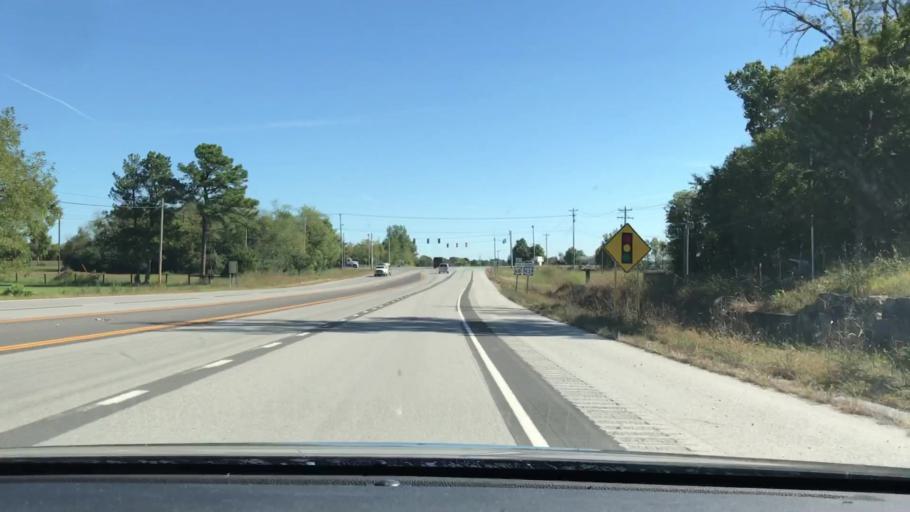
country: US
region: Kentucky
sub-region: Logan County
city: Russellville
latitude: 36.8387
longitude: -86.9213
